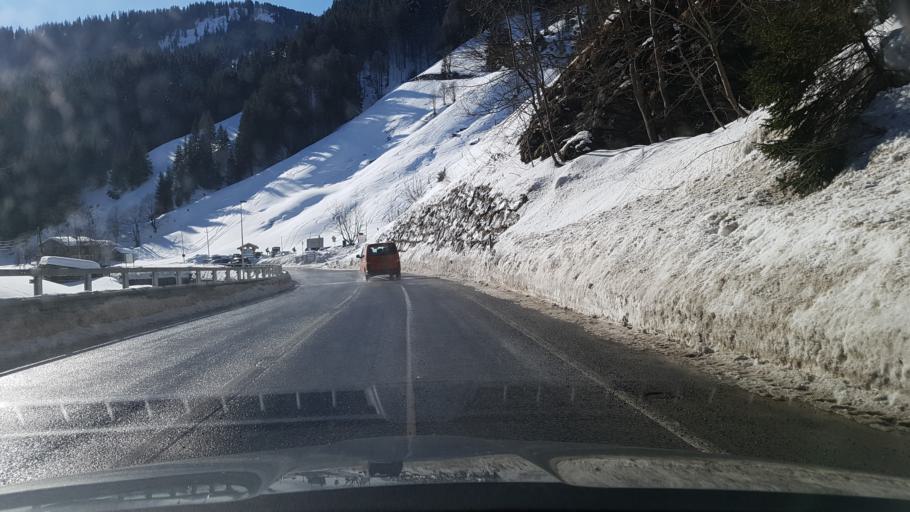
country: AT
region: Salzburg
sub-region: Politischer Bezirk Zell am See
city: Dienten am Hochkonig
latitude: 47.3775
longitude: 13.0016
